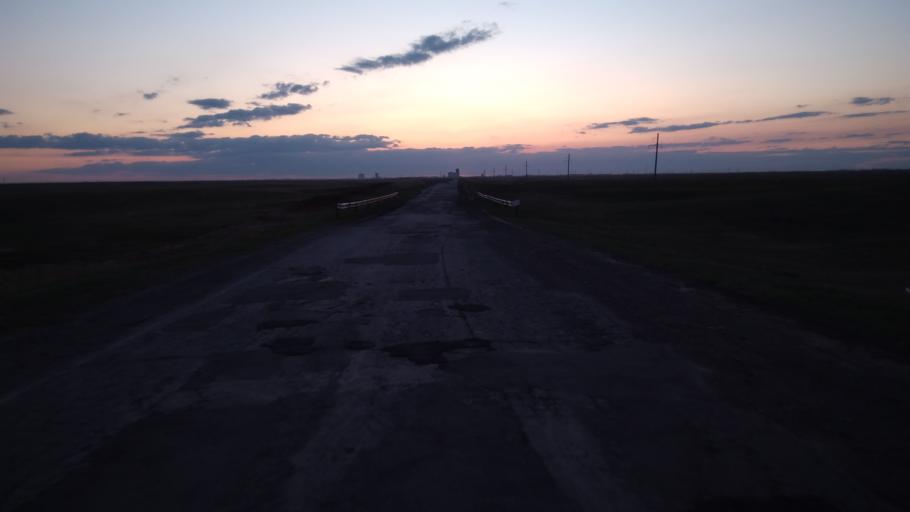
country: RU
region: Chelyabinsk
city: Troitsk
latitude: 54.0880
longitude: 61.6548
